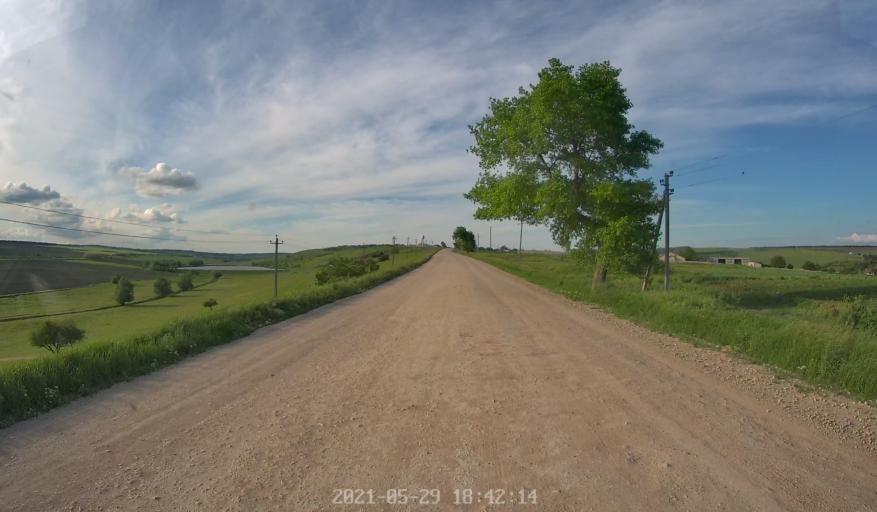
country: MD
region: Chisinau
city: Singera
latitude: 46.8108
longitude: 28.9615
